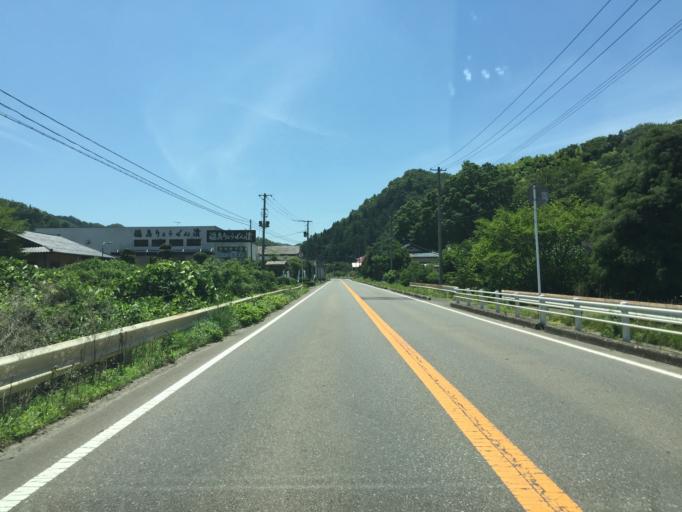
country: JP
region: Fukushima
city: Hobaramachi
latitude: 37.7644
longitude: 140.5662
